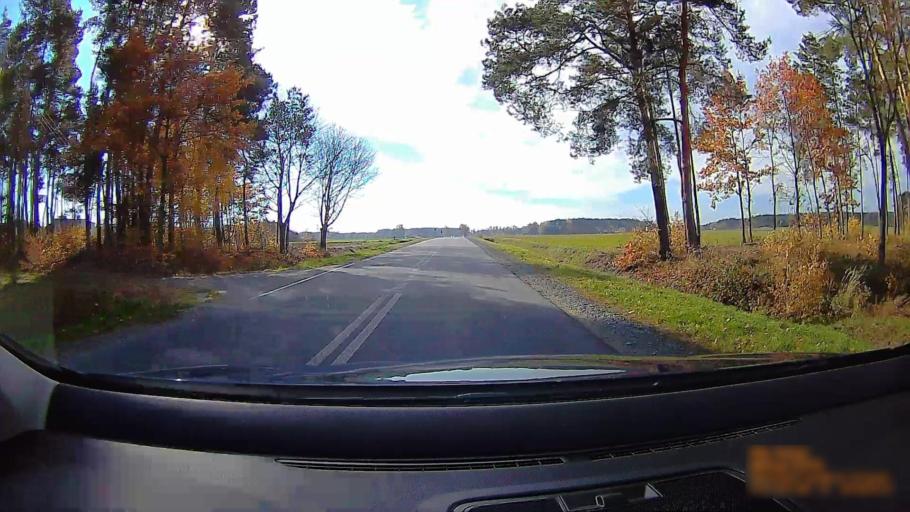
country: PL
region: Greater Poland Voivodeship
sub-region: Powiat ostrzeszowski
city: Doruchow
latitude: 51.3853
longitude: 18.0475
